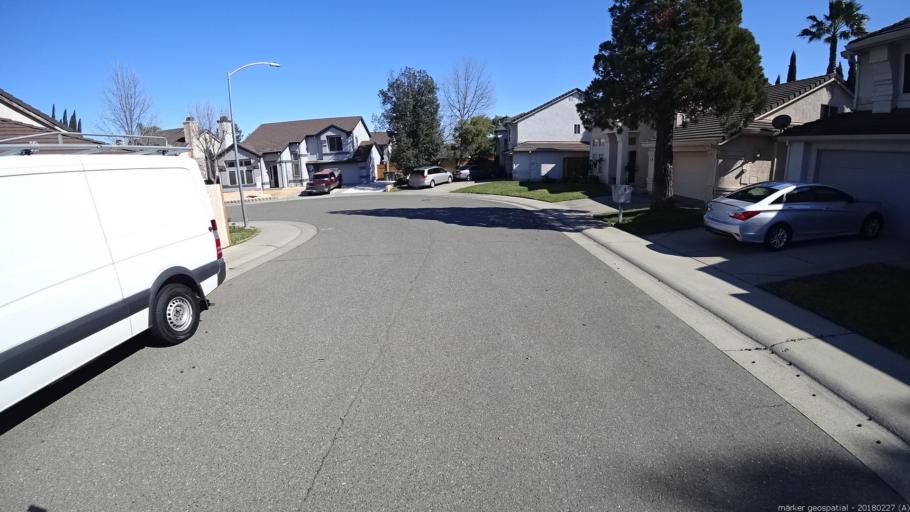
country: US
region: California
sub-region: Sacramento County
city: North Highlands
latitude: 38.7239
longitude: -121.3804
